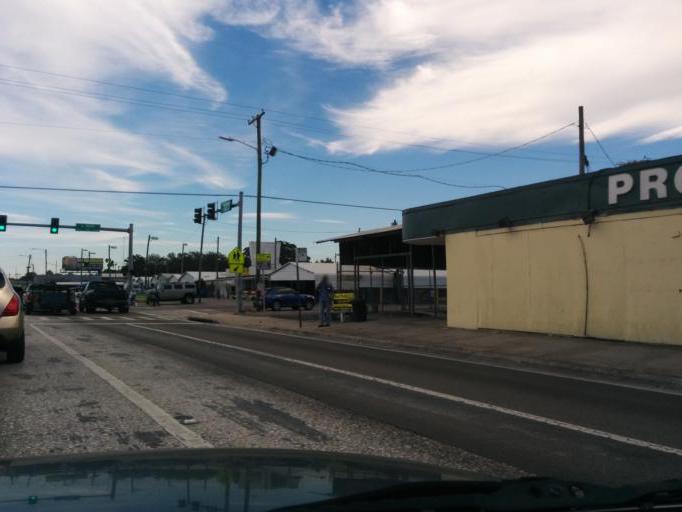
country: US
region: Florida
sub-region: Hillsborough County
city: East Lake-Orient Park
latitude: 27.9960
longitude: -82.4269
